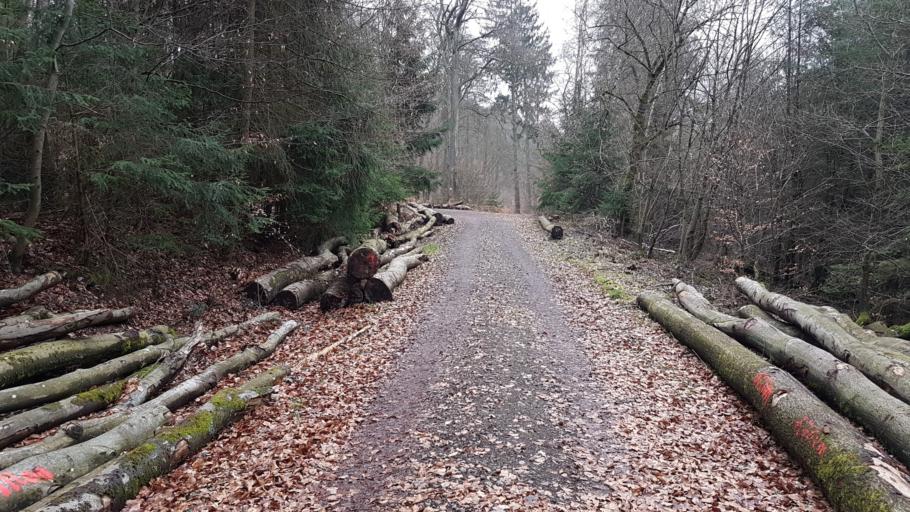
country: DE
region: Saarland
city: Sankt Wendel
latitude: 49.4411
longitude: 7.1754
